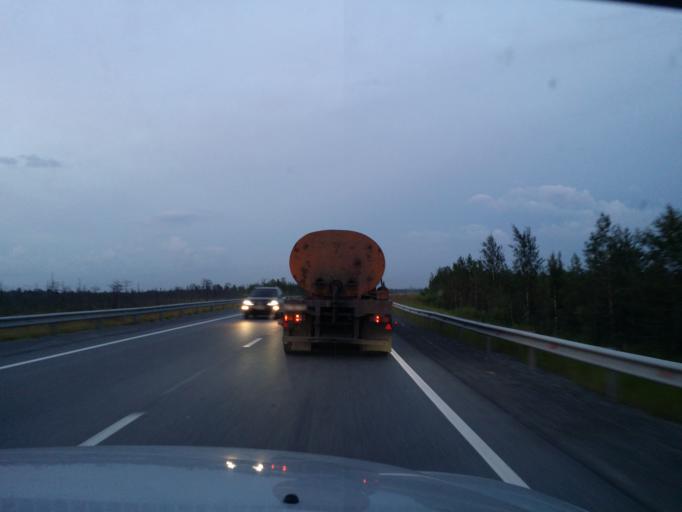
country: RU
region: Khanty-Mansiyskiy Avtonomnyy Okrug
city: Poykovskiy
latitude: 61.3559
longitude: 73.3068
